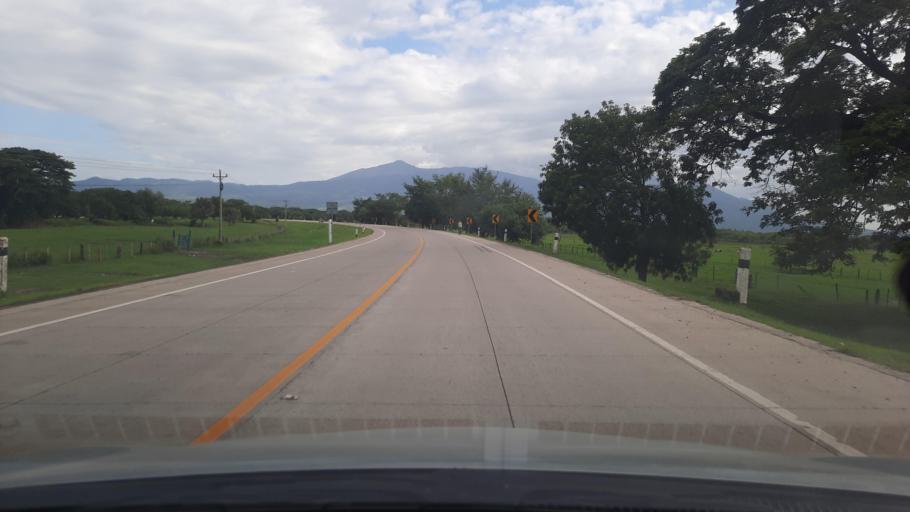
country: NI
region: Chinandega
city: Somotillo
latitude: 12.8147
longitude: -86.9017
